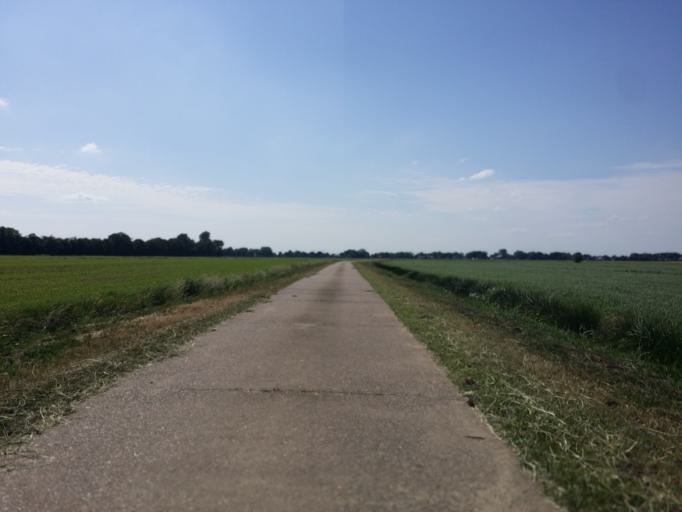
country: DE
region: Lower Saxony
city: Elsfleth
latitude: 53.2022
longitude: 8.4100
